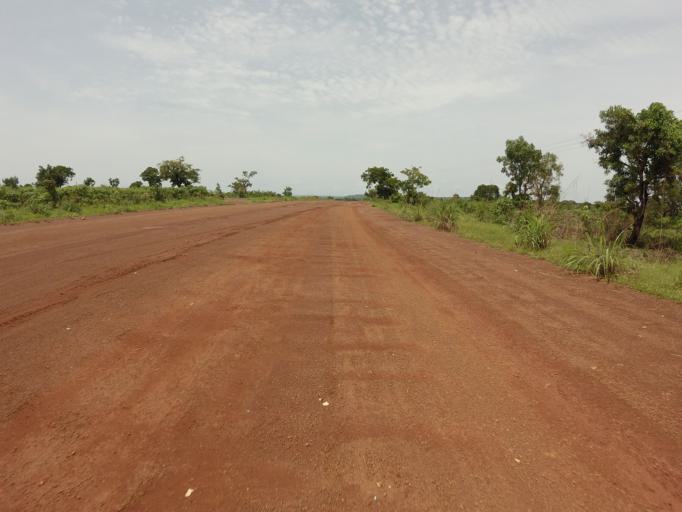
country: GH
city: Kpandae
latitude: 8.7496
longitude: 0.0739
